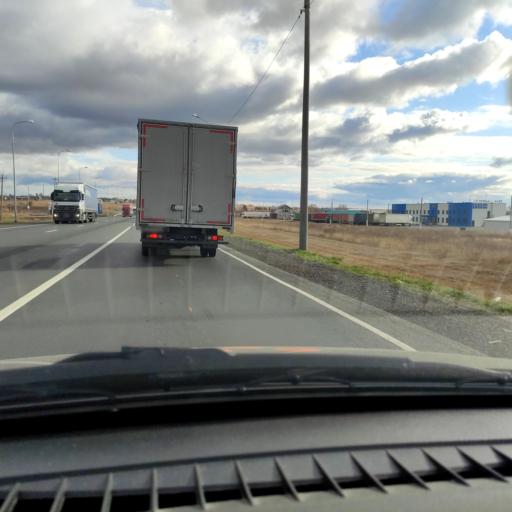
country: RU
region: Samara
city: Syzran'
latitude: 53.2106
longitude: 48.4801
